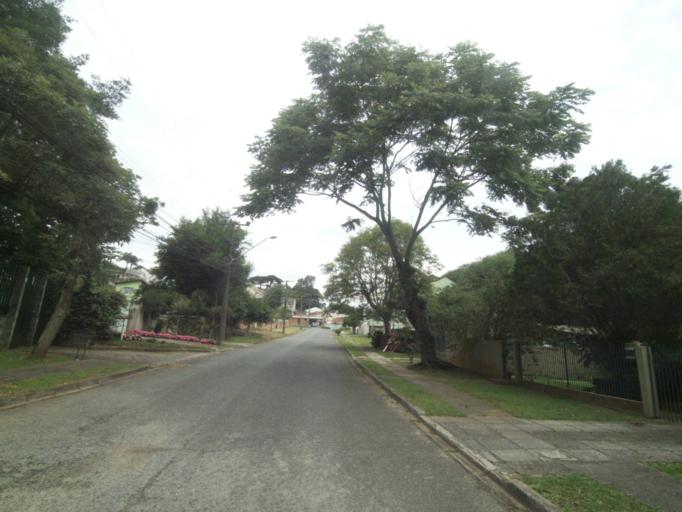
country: BR
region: Parana
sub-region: Curitiba
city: Curitiba
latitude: -25.4132
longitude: -49.3033
